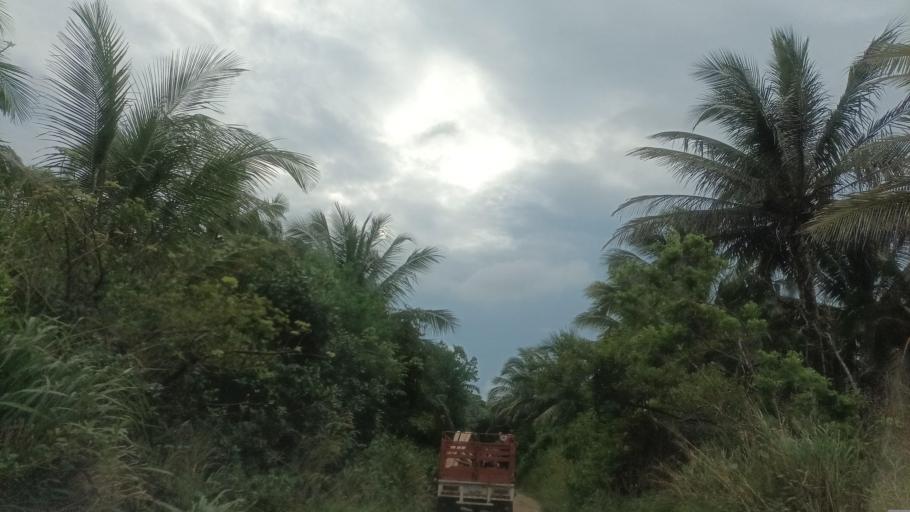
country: MX
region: Veracruz
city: Allende
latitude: 18.1777
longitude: -94.2754
